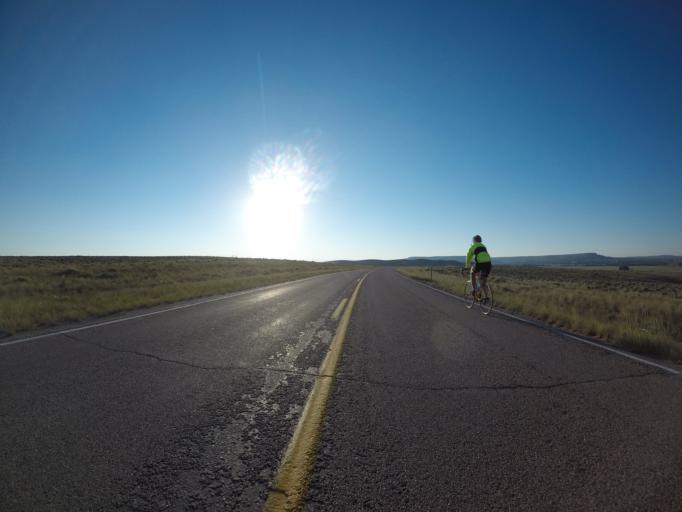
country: US
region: Wyoming
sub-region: Sublette County
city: Marbleton
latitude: 42.5806
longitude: -109.9948
